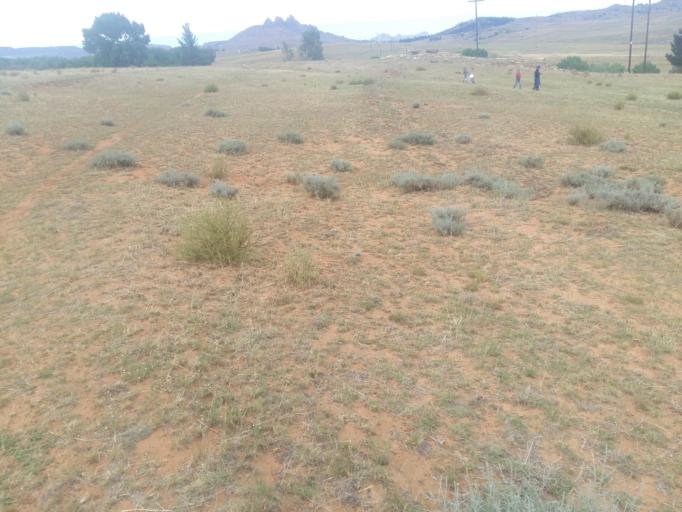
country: LS
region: Mafeteng
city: Mafeteng
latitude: -29.6944
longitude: 27.4301
